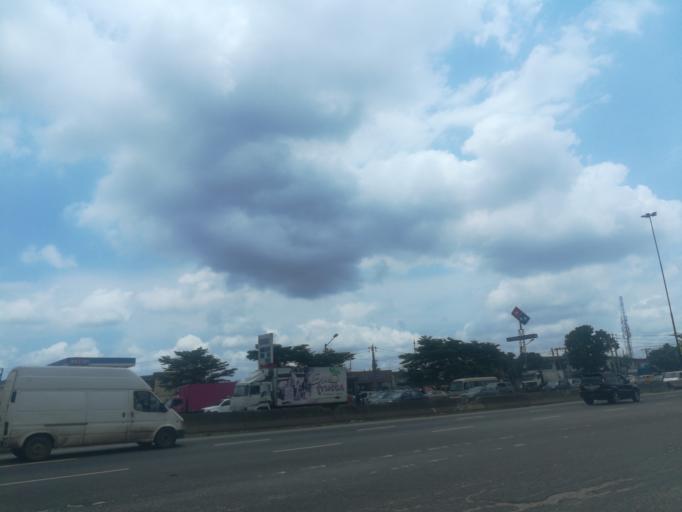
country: NG
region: Lagos
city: Somolu
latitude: 6.5494
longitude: 3.3887
